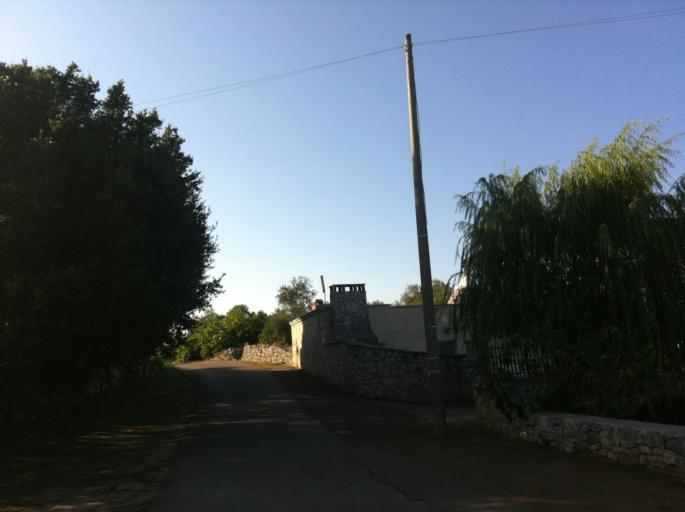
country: IT
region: Apulia
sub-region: Provincia di Bari
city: Putignano
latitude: 40.8262
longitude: 17.1388
